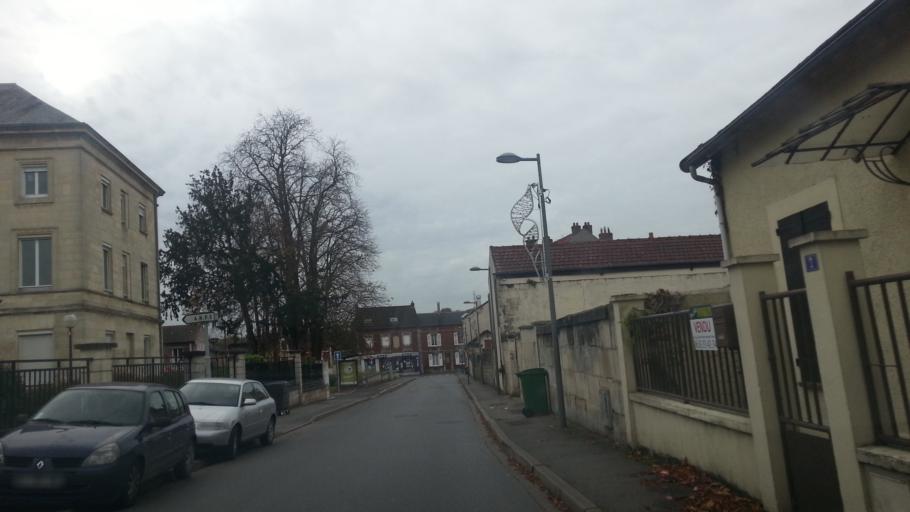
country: FR
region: Picardie
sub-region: Departement de l'Oise
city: Montataire
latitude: 49.2582
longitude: 2.4311
